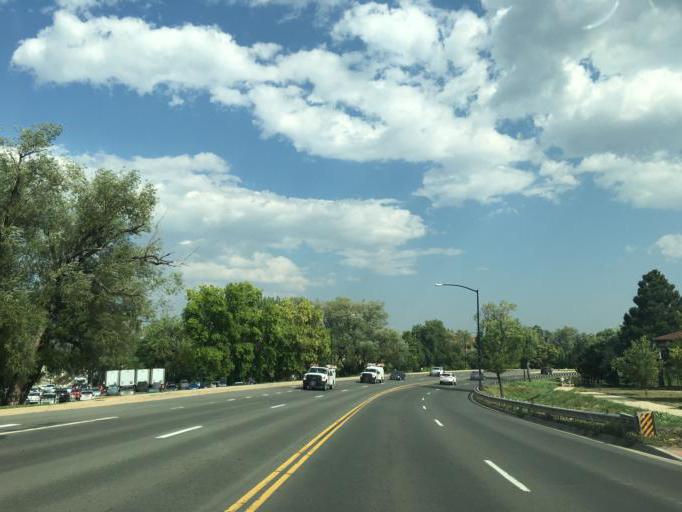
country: US
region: Colorado
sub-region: Boulder County
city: Boulder
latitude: 40.0032
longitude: -105.2670
